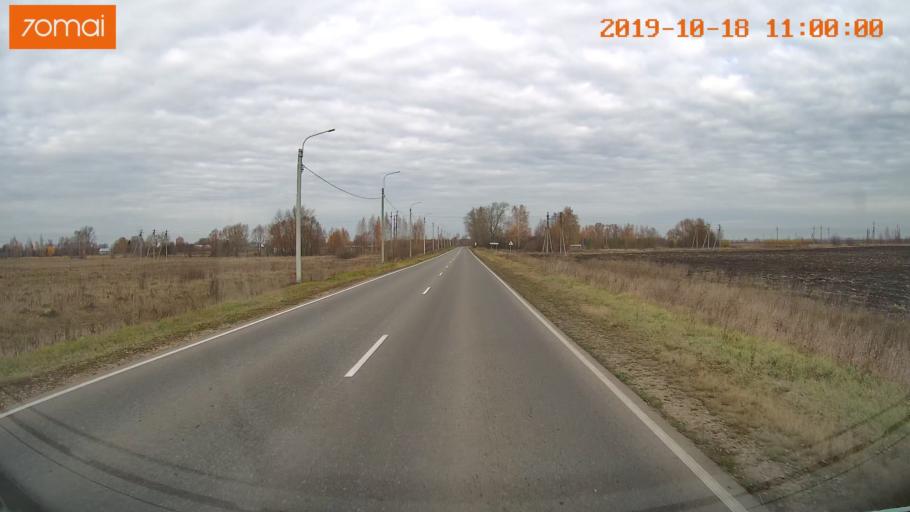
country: RU
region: Tula
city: Yepifan'
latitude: 53.8377
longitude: 38.5541
